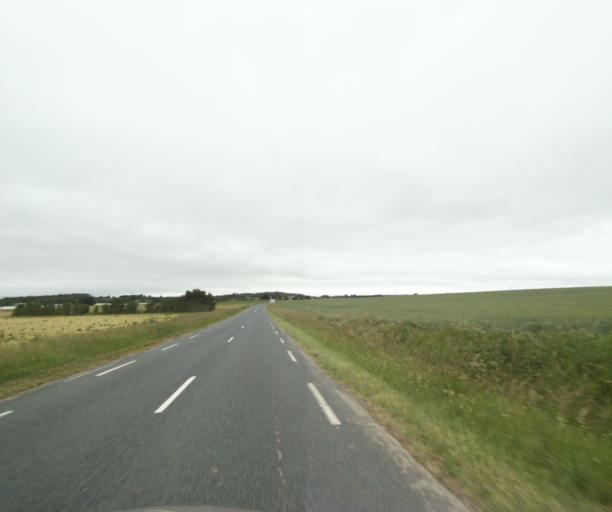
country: FR
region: Rhone-Alpes
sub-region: Departement de l'Ain
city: Mionnay
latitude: 45.8622
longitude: 4.9220
